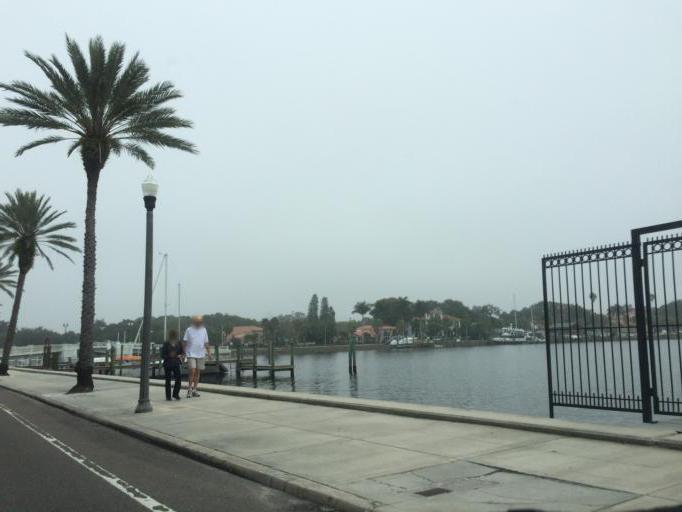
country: US
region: Florida
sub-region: Pinellas County
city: Saint Petersburg
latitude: 27.7909
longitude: -82.6264
